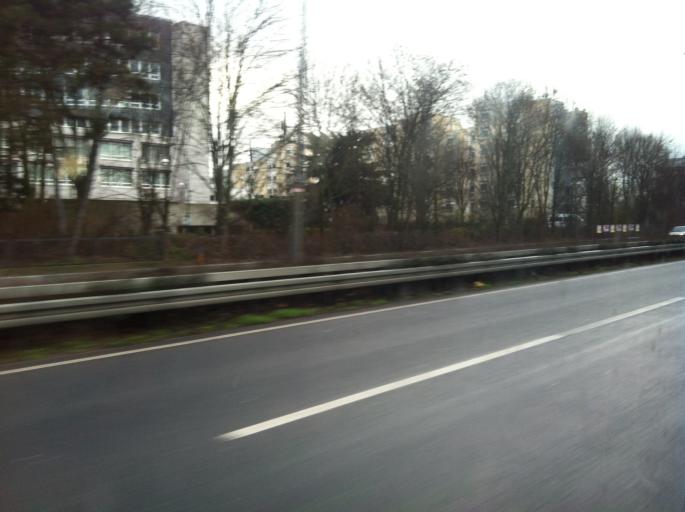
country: DE
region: Hesse
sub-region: Regierungsbezirk Darmstadt
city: Wiesbaden
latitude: 50.0657
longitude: 8.2702
